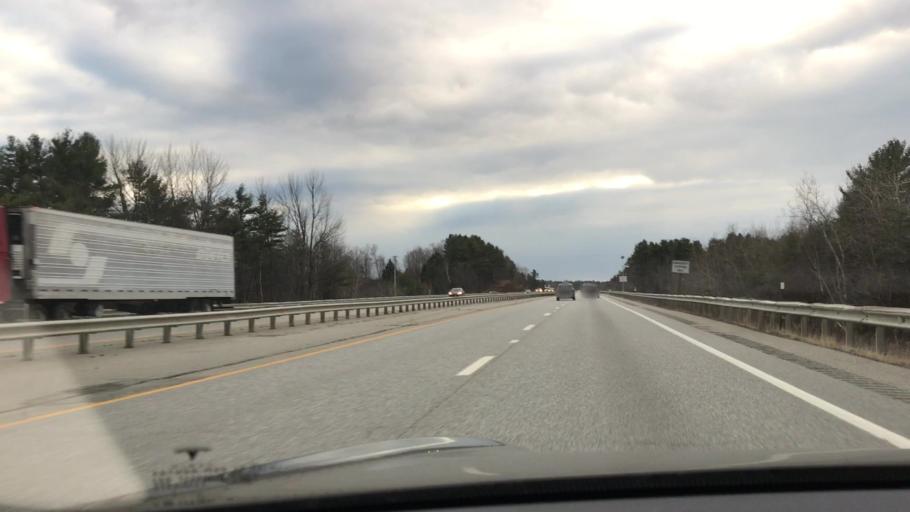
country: US
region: Maine
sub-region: Kennebec County
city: Farmingdale
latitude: 44.2471
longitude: -69.8077
